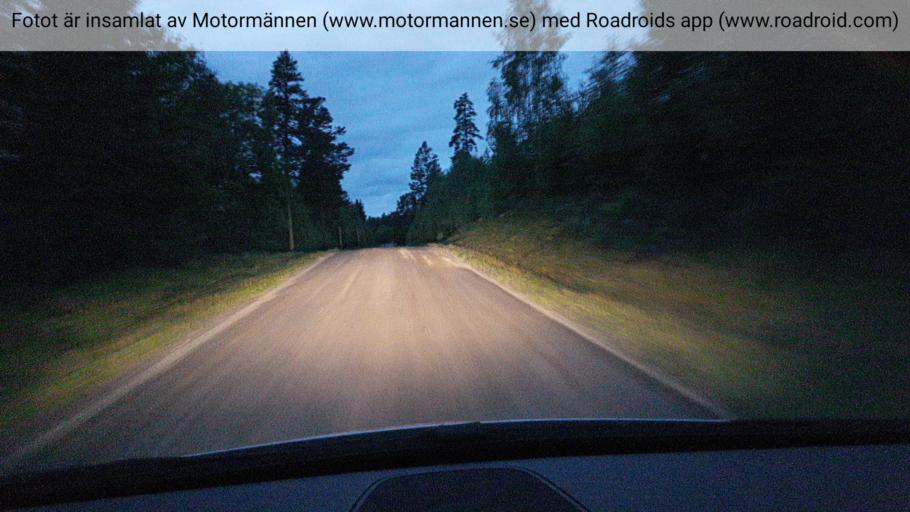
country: SE
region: Jaemtland
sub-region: Braecke Kommun
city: Braecke
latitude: 63.1974
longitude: 15.4628
